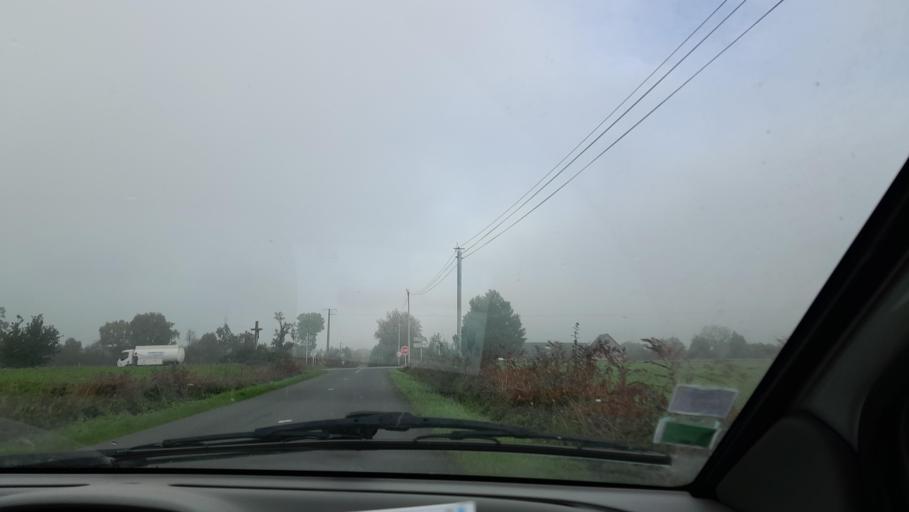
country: FR
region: Pays de la Loire
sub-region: Departement de la Mayenne
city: Saint-Pierre-la-Cour
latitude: 48.1419
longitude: -1.0286
